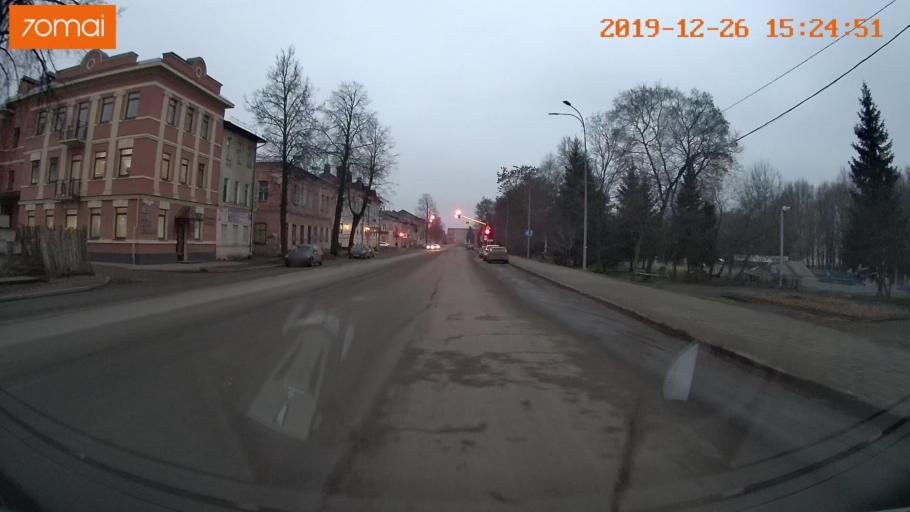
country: RU
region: Jaroslavl
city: Rybinsk
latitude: 58.0517
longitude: 38.8442
